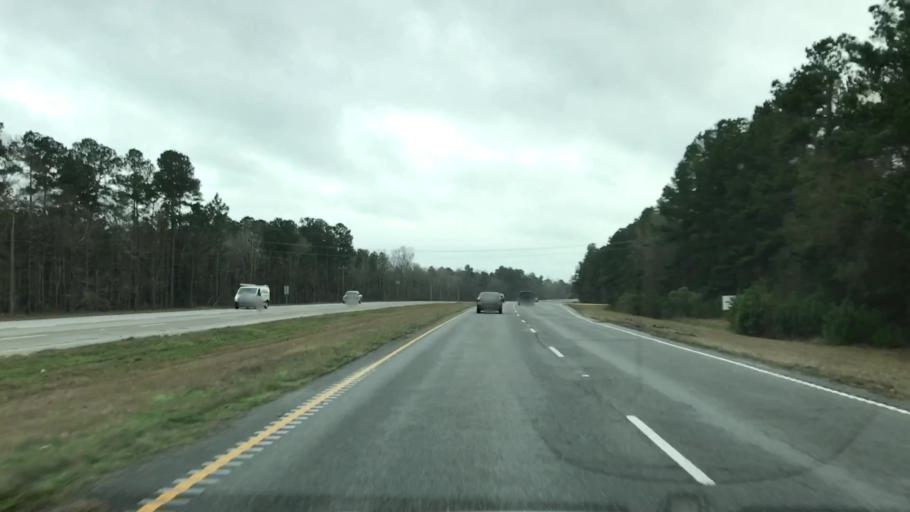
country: US
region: South Carolina
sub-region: Berkeley County
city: Moncks Corner
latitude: 33.1218
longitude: -80.0287
